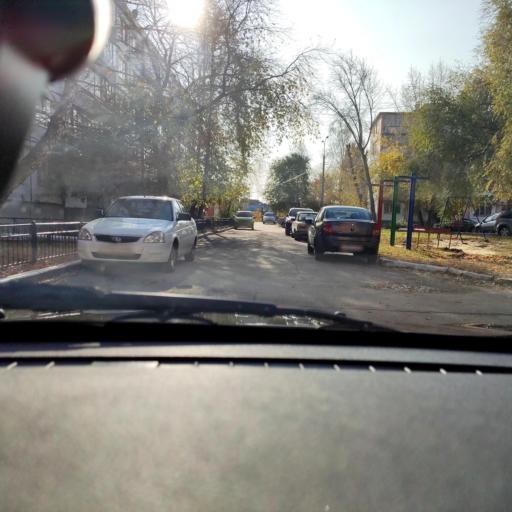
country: RU
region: Samara
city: Tol'yatti
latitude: 53.5288
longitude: 49.4021
